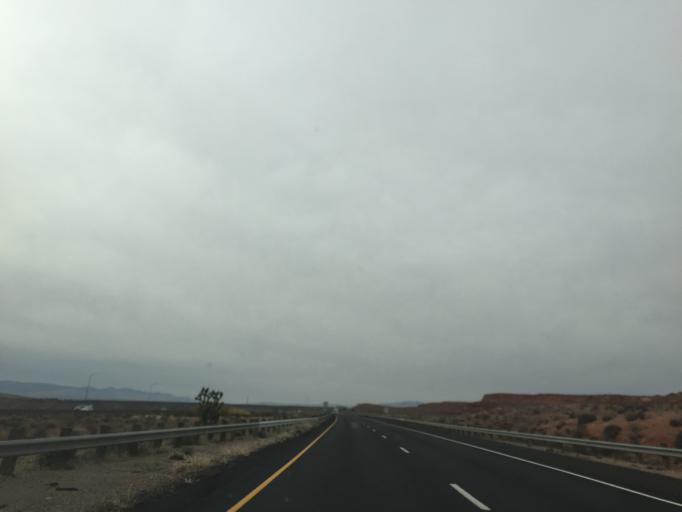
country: US
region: Utah
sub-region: Washington County
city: Washington
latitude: 37.1701
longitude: -113.4445
